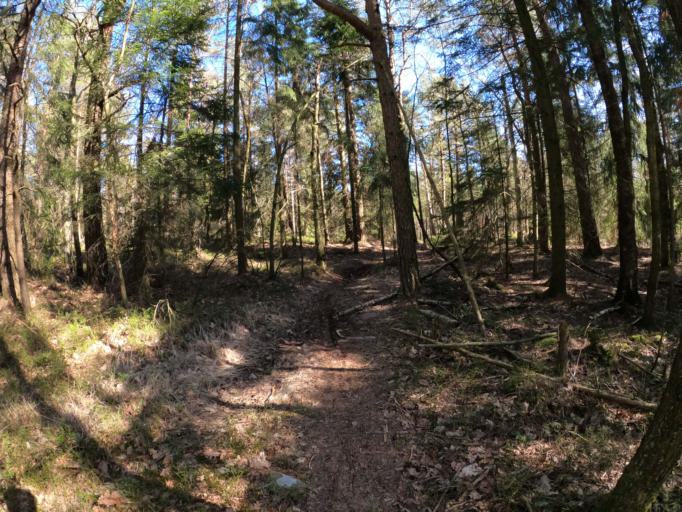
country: SE
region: Vaestra Goetaland
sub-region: Harryda Kommun
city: Molnlycke
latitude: 57.6253
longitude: 12.1228
